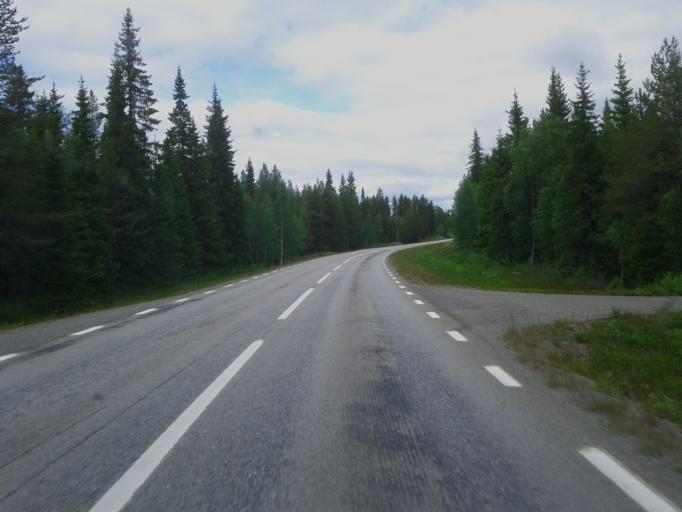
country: SE
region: Vaesterbotten
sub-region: Storumans Kommun
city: Fristad
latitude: 65.3679
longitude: 16.5201
